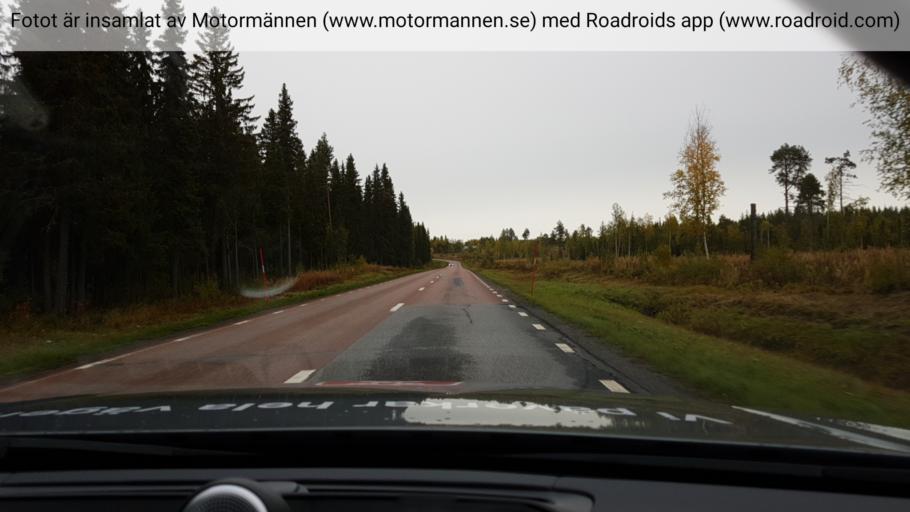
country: SE
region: Jaemtland
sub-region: Stroemsunds Kommun
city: Stroemsund
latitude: 63.8063
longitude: 15.5193
